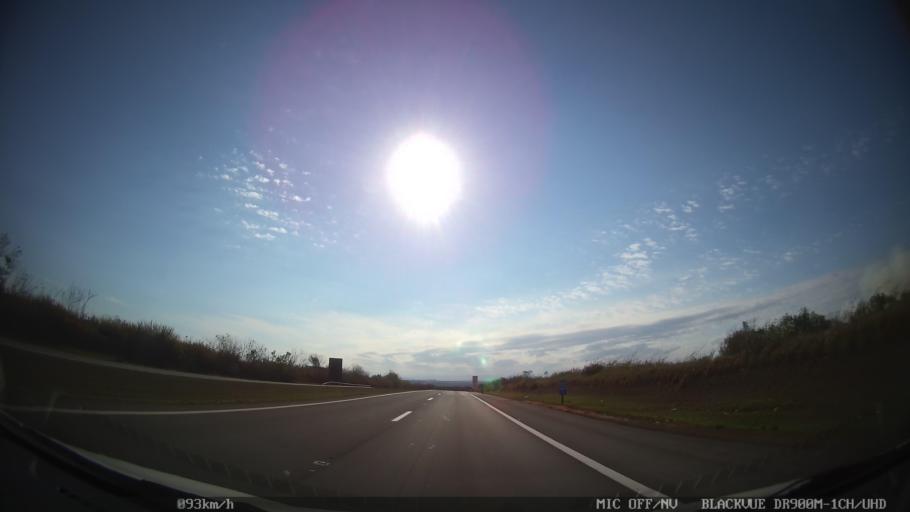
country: BR
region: Sao Paulo
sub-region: Piracicaba
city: Piracicaba
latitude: -22.7135
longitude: -47.6080
